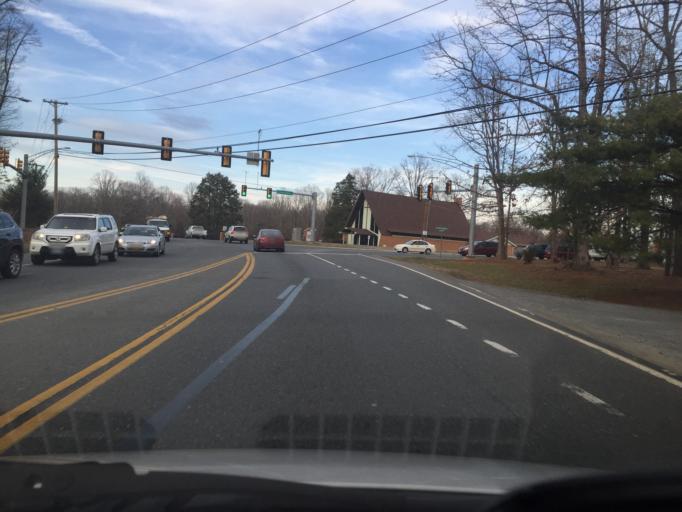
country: US
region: Virginia
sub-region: Bedford County
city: Forest
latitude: 37.3515
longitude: -79.2814
